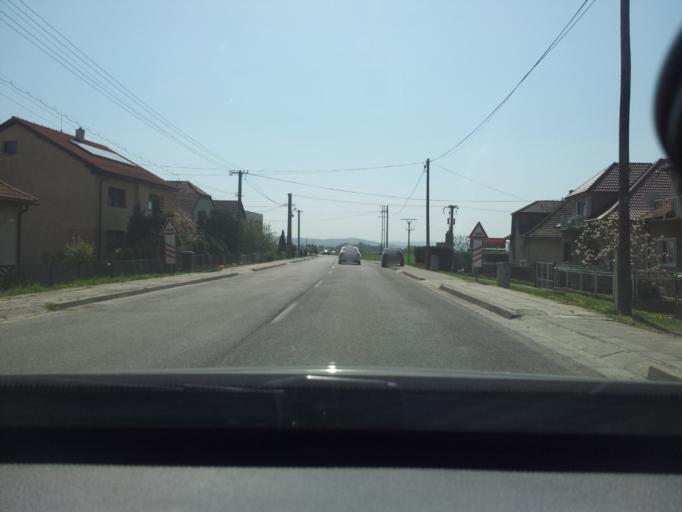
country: SK
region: Nitriansky
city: Banovce nad Bebravou
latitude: 48.6639
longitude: 18.2625
